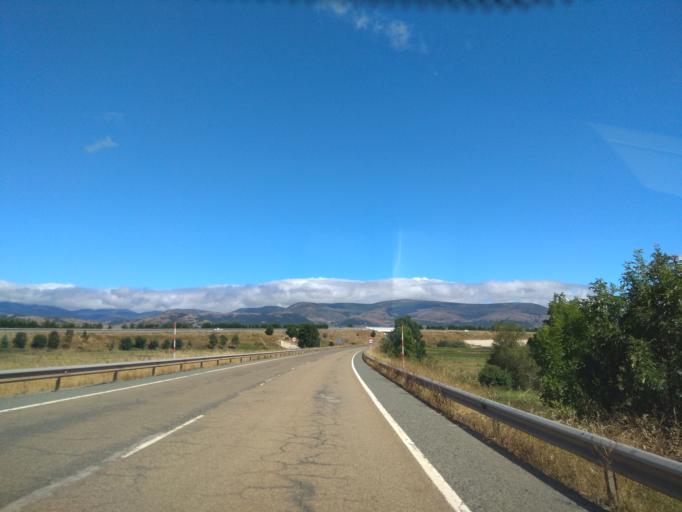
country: ES
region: Cantabria
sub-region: Provincia de Cantabria
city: Villaescusa
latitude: 42.9710
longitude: -4.1531
